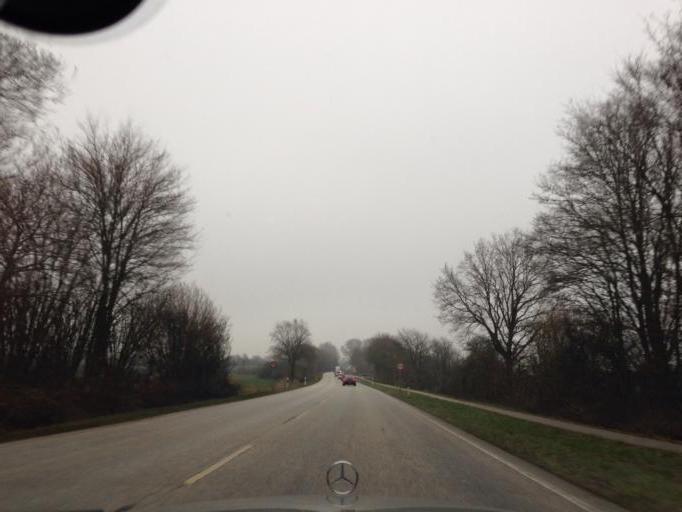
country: DE
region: Schleswig-Holstein
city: Kirchbarkau
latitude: 54.2174
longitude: 10.1470
